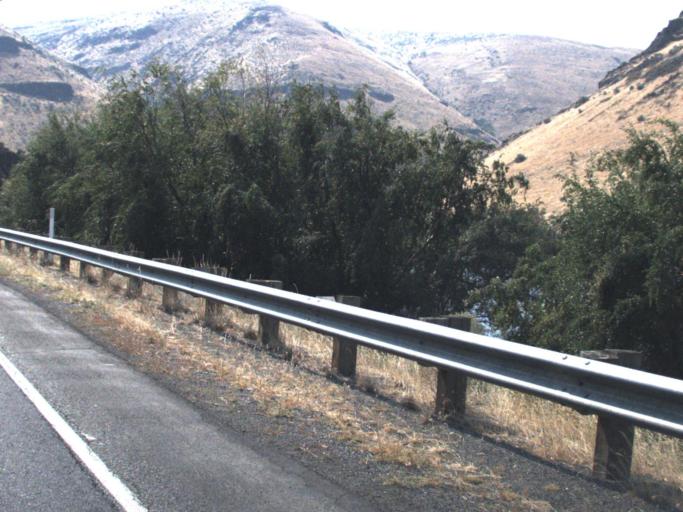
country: US
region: Washington
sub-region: Kittitas County
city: Kittitas
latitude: 46.8572
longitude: -120.4822
